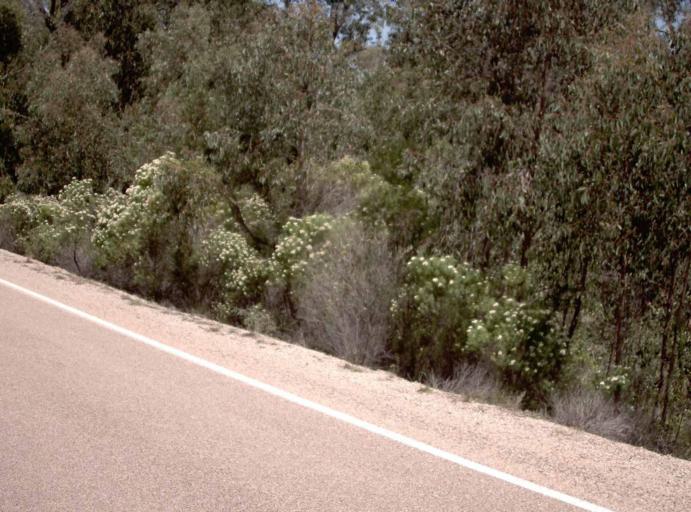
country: AU
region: Victoria
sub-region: East Gippsland
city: Lakes Entrance
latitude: -37.6109
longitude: 147.8809
